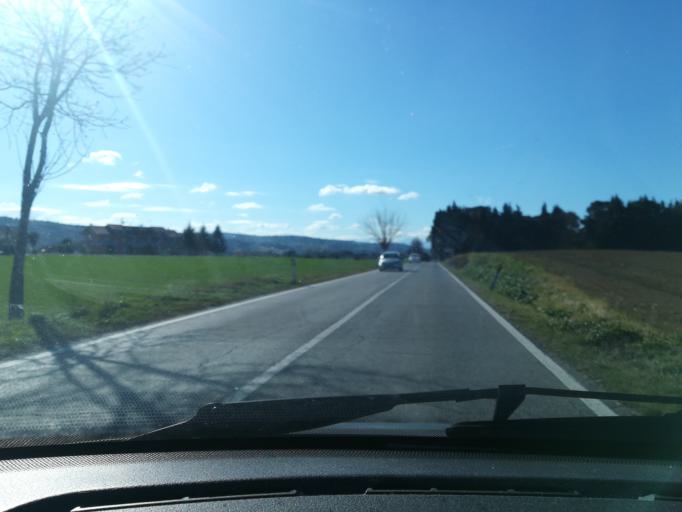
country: IT
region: The Marches
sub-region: Provincia di Macerata
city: Montecassiano
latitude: 43.3517
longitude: 13.4368
